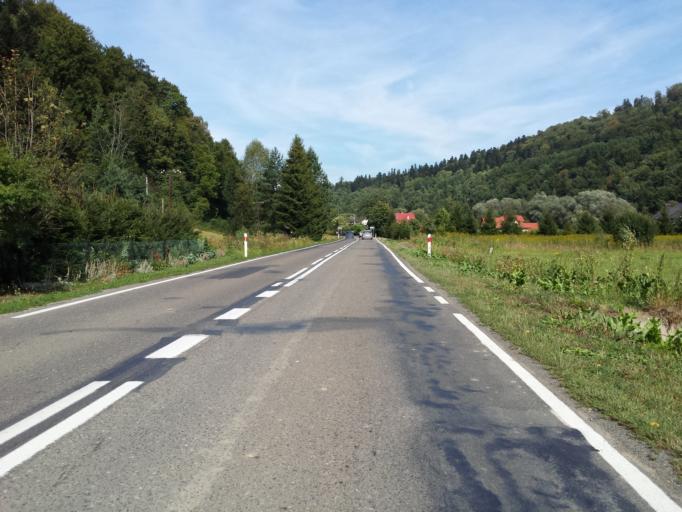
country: PL
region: Subcarpathian Voivodeship
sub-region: Powiat leski
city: Lesko
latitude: 49.4459
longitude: 22.3482
